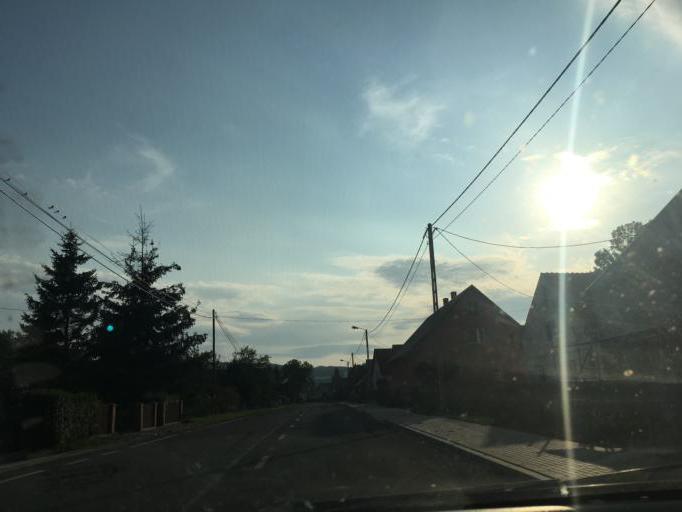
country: PL
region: Opole Voivodeship
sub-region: Powiat nyski
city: Kamienica
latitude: 50.4477
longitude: 16.9418
